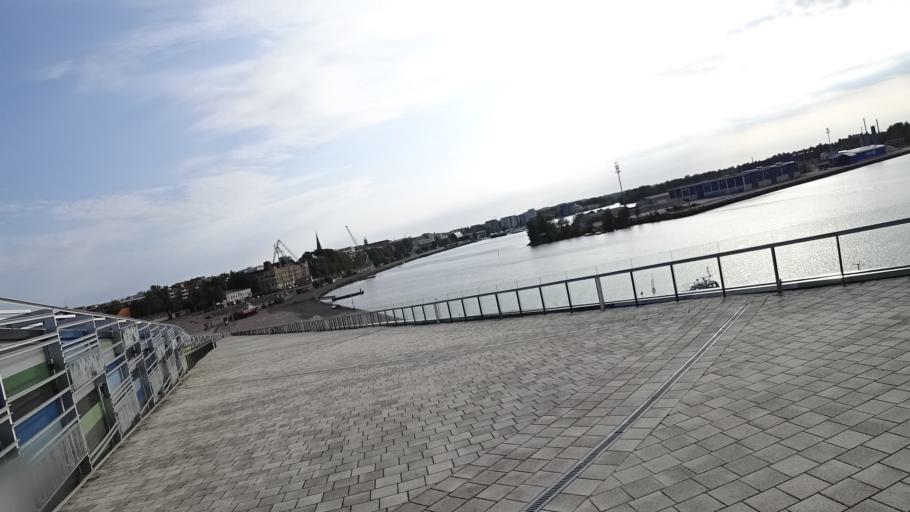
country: FI
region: Kymenlaakso
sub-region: Kotka-Hamina
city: Kotka
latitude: 60.4728
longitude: 26.9448
